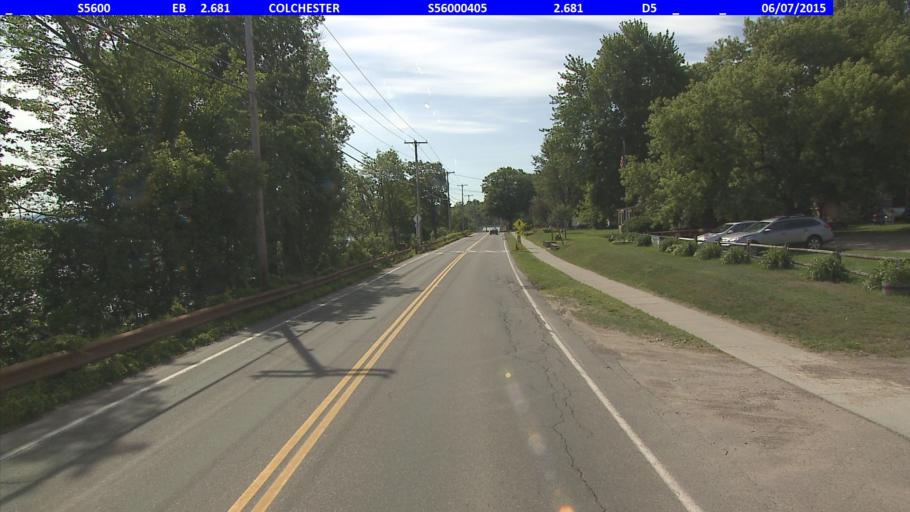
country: US
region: Vermont
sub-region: Chittenden County
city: Winooski
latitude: 44.5492
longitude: -73.2242
